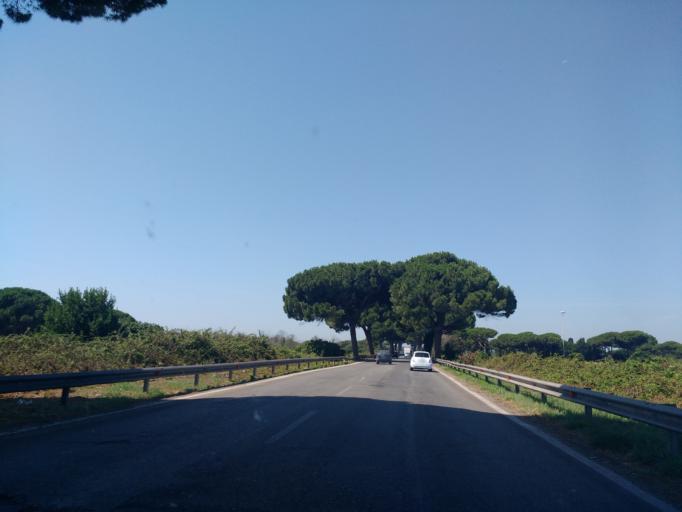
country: IT
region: Latium
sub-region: Citta metropolitana di Roma Capitale
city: Lido di Ostia
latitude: 41.7539
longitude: 12.2955
